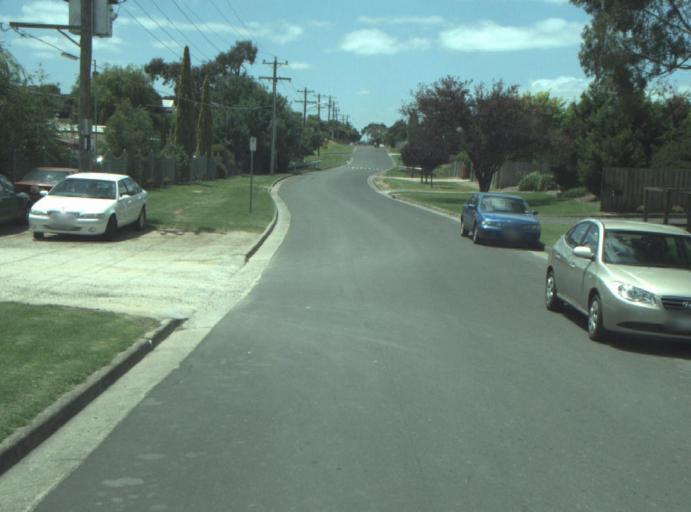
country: AU
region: Victoria
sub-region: Greater Geelong
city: Breakwater
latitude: -38.1880
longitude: 144.3494
